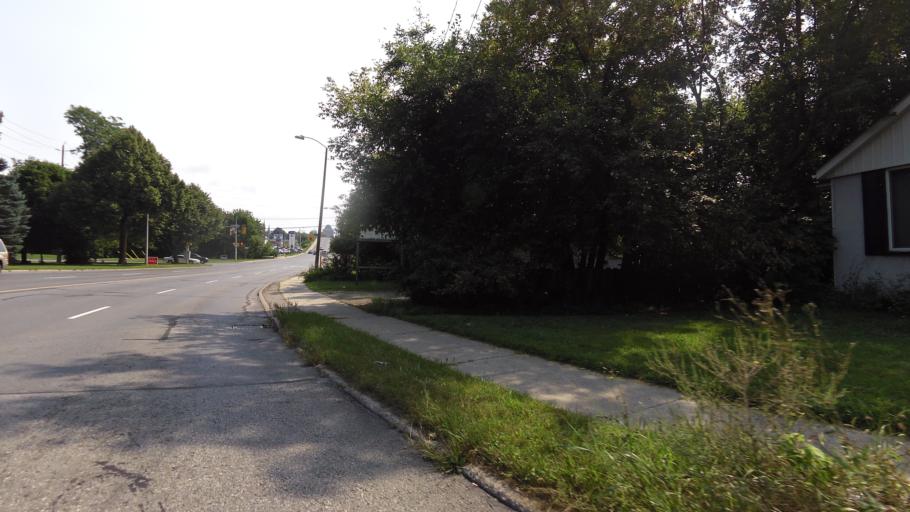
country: CA
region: Ontario
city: Brockville
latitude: 44.5964
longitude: -75.6928
